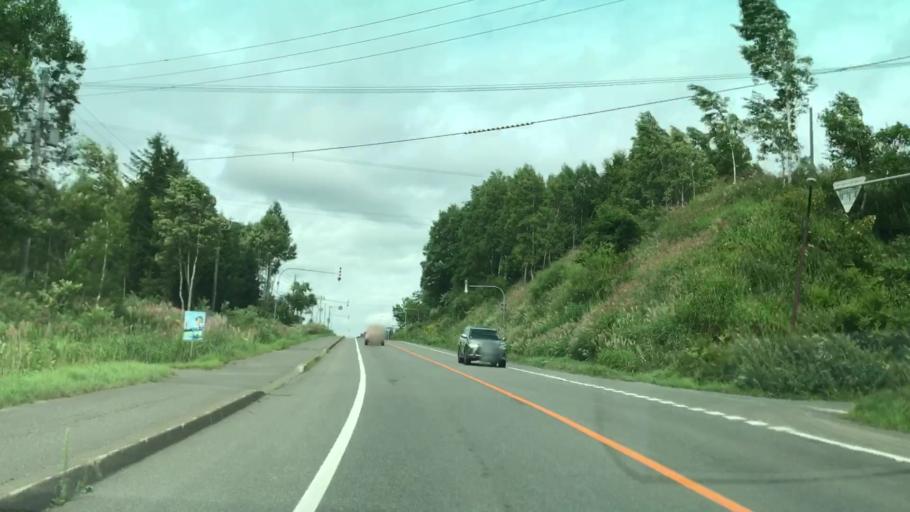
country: JP
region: Hokkaido
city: Niseko Town
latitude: 42.9127
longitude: 140.7524
